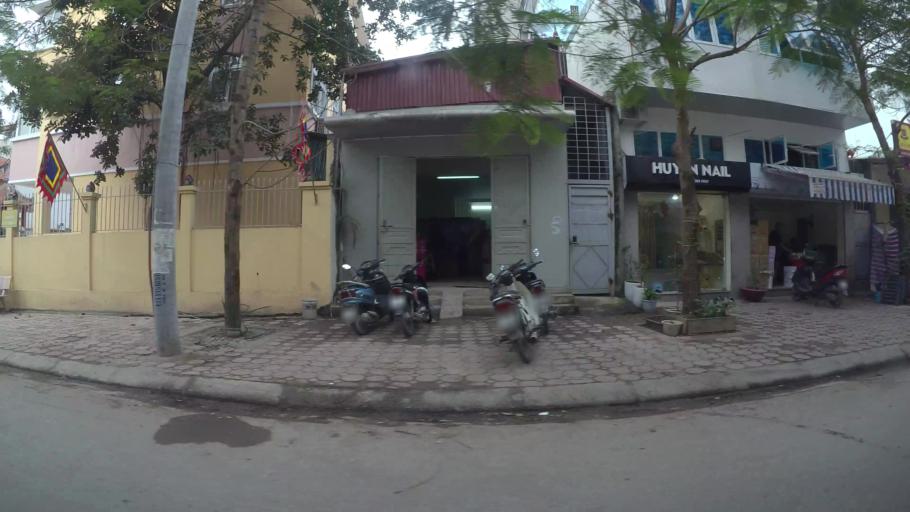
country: VN
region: Ha Noi
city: Dong Da
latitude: 21.0385
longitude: 105.8233
